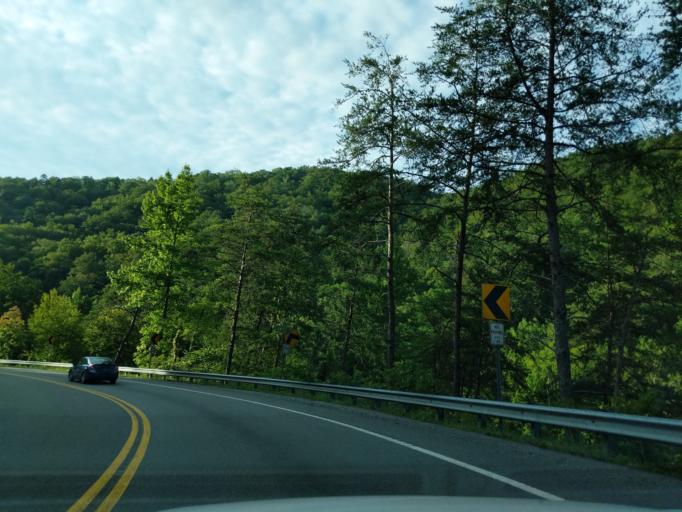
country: US
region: Tennessee
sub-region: Polk County
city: Benton
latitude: 35.0821
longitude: -84.5292
